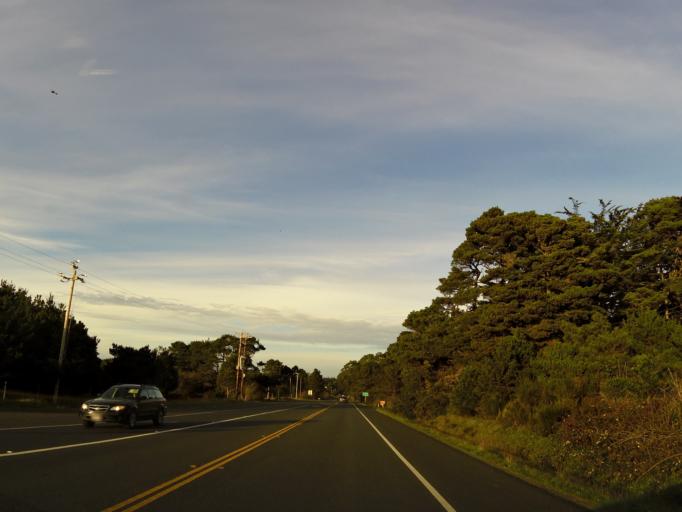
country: US
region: California
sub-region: Mendocino County
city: Fort Bragg
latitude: 39.3836
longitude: -123.8138
